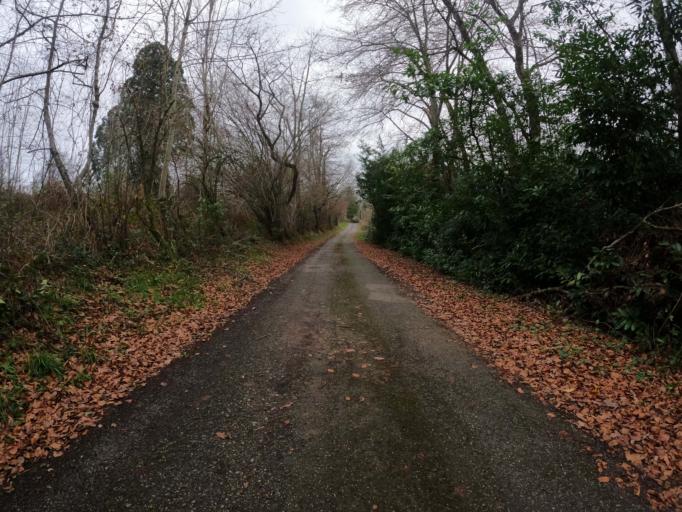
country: FR
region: Aquitaine
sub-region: Departement des Pyrenees-Atlantiques
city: Mazeres-Lezons
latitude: 43.2647
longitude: -0.3510
